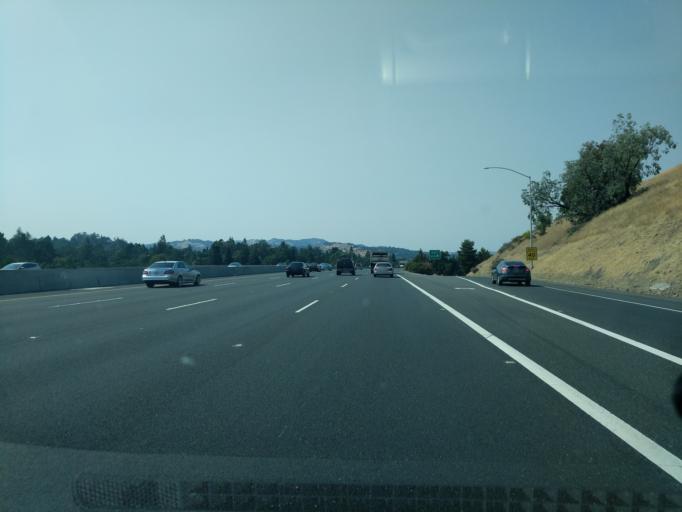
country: US
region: California
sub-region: Contra Costa County
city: Alamo
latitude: 37.8768
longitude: -122.0467
